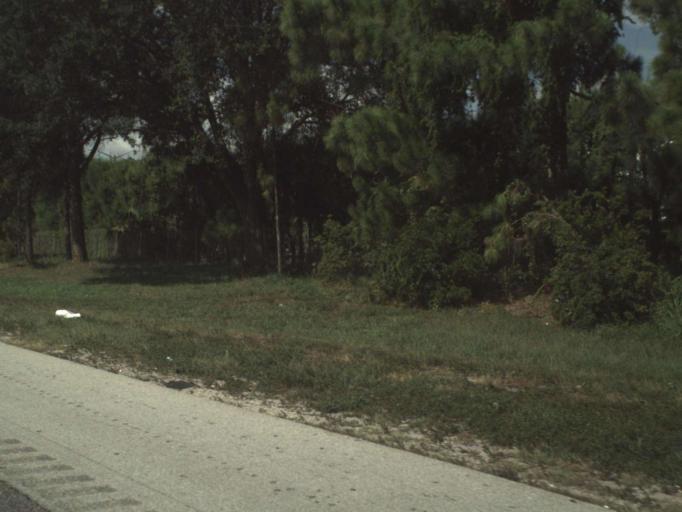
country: US
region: Florida
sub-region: Palm Beach County
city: Mangonia Park
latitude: 26.7388
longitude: -80.0910
